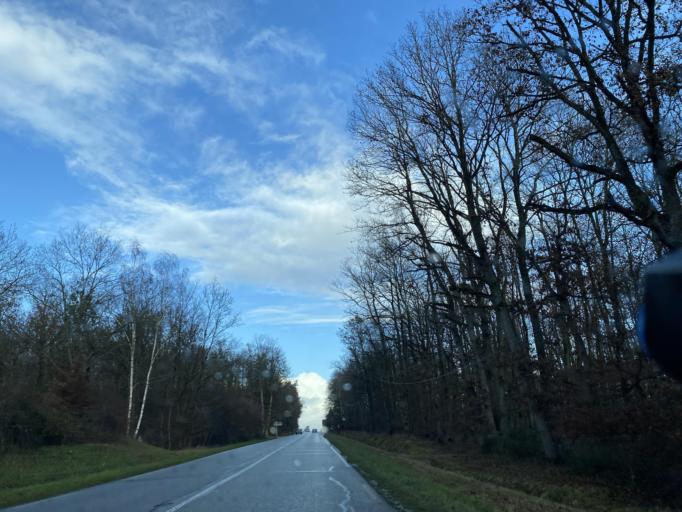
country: FR
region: Haute-Normandie
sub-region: Departement de l'Eure
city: Evreux
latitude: 48.9780
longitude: 1.1505
